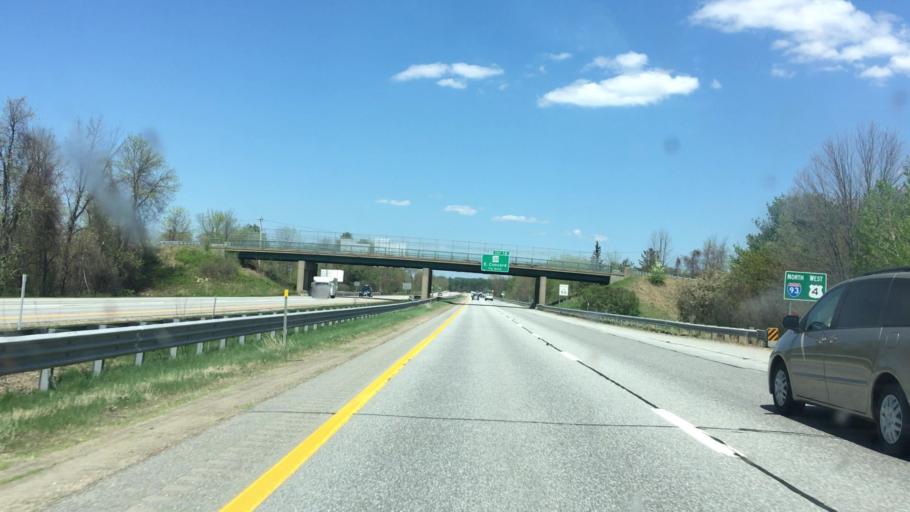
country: US
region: New Hampshire
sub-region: Merrimack County
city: Concord
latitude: 43.2226
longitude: -71.5342
